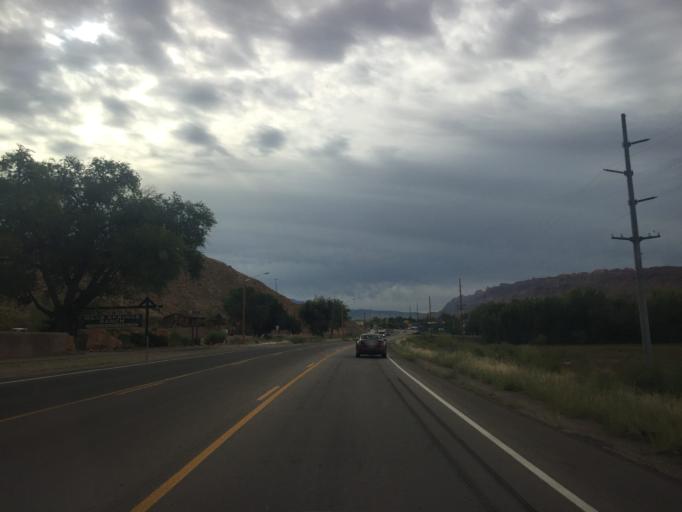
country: US
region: Utah
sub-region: Grand County
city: Moab
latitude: 38.5925
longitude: -109.5647
